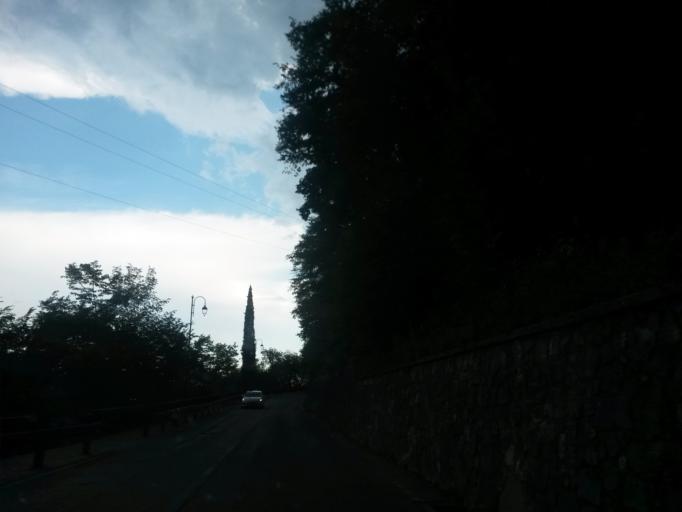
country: IT
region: Lombardy
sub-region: Provincia di Brescia
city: Gardola
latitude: 45.7410
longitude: 10.7289
